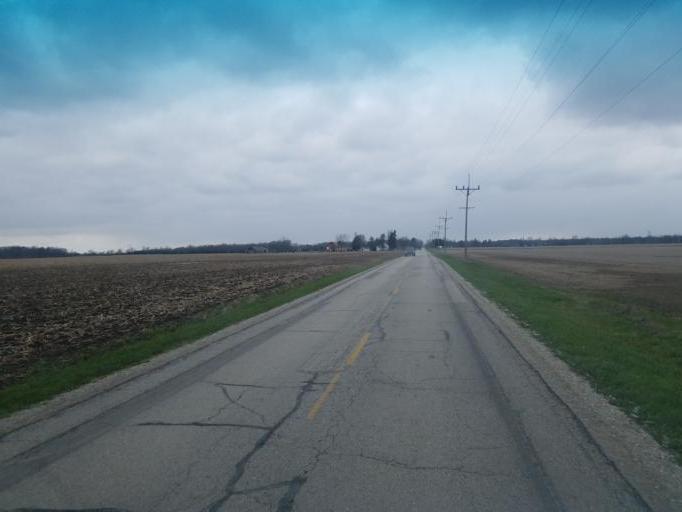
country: US
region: Ohio
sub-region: Marion County
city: Prospect
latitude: 40.5061
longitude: -83.1513
